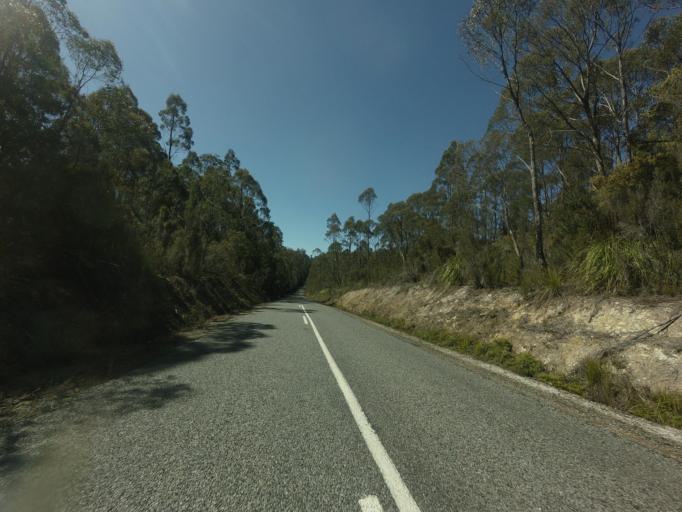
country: AU
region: Tasmania
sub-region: Derwent Valley
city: New Norfolk
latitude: -42.7543
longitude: 146.4102
